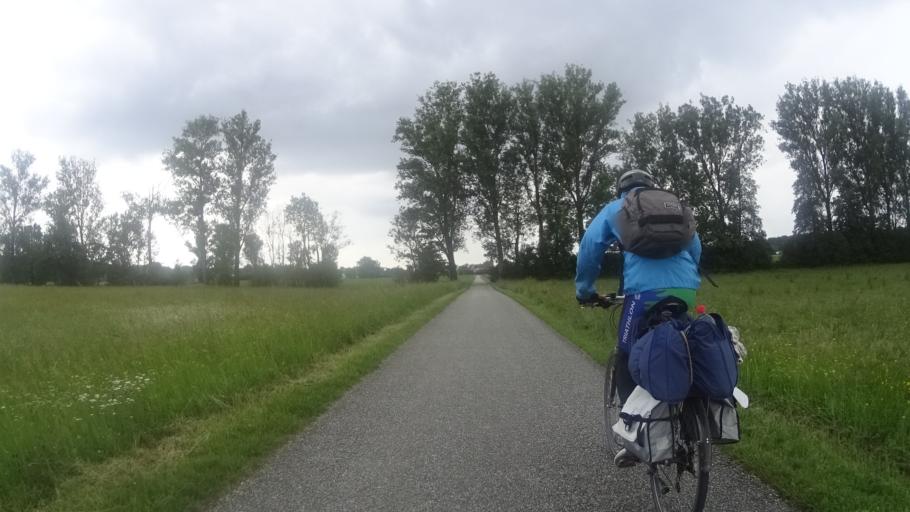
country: DE
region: Bavaria
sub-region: Lower Bavaria
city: Hebertsfelden
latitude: 48.4182
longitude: 12.8439
